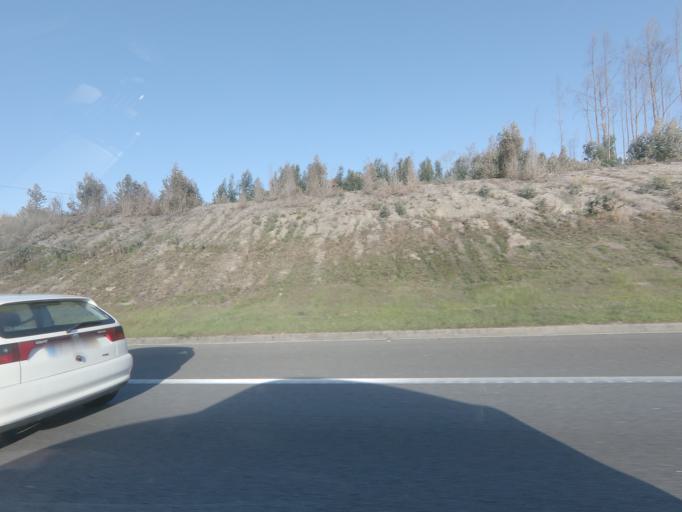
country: PT
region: Aveiro
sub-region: Oliveira do Bairro
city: Oia
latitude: 40.5766
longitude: -8.5617
